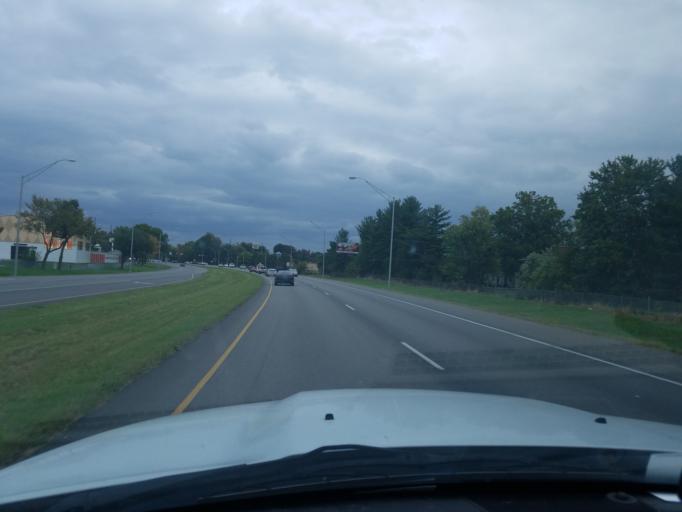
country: US
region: Indiana
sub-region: Vanderburgh County
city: Evansville
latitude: 37.9520
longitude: -87.5422
